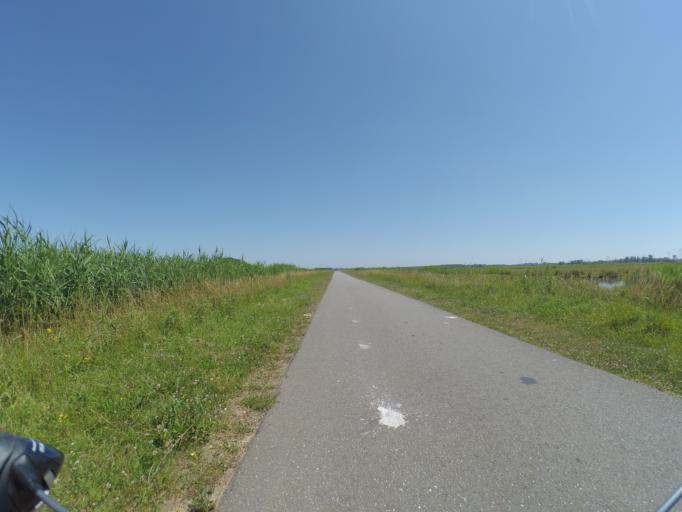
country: NL
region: South Holland
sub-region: Gemeente Sliedrecht
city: Sliedrecht
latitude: 51.7709
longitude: 4.7960
